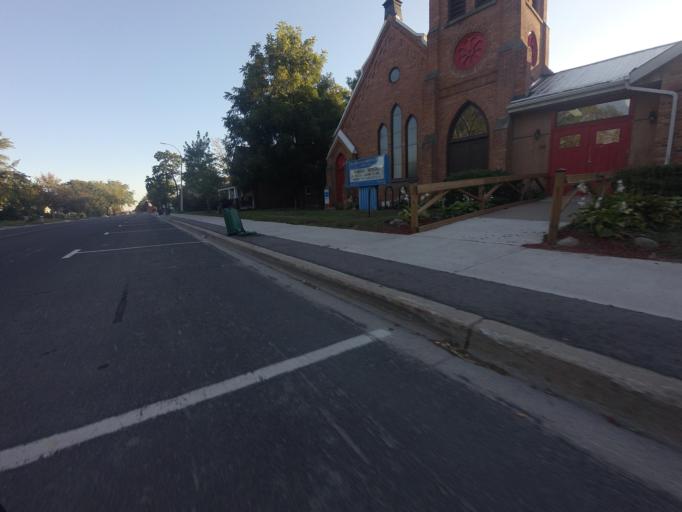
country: CA
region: Ontario
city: Bradford West Gwillimbury
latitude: 44.0259
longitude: -79.8065
